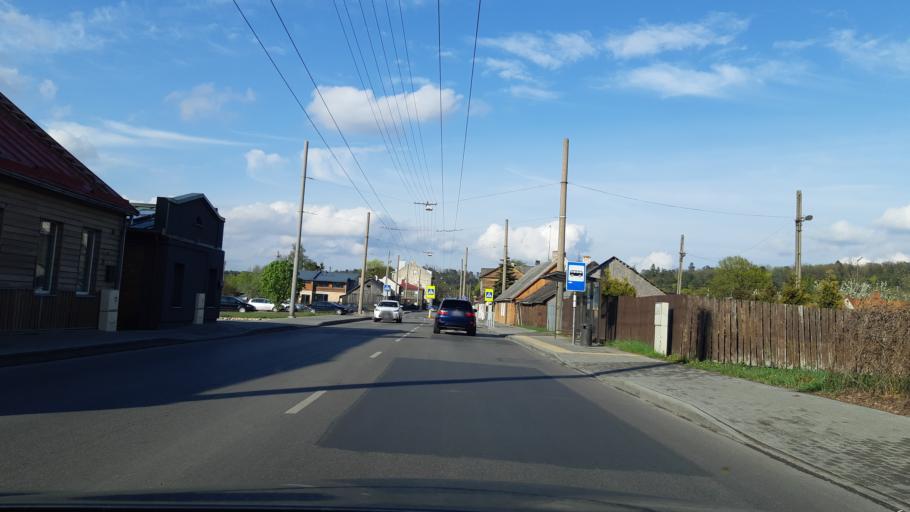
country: LT
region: Kauno apskritis
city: Dainava (Kaunas)
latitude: 54.8653
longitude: 23.9671
